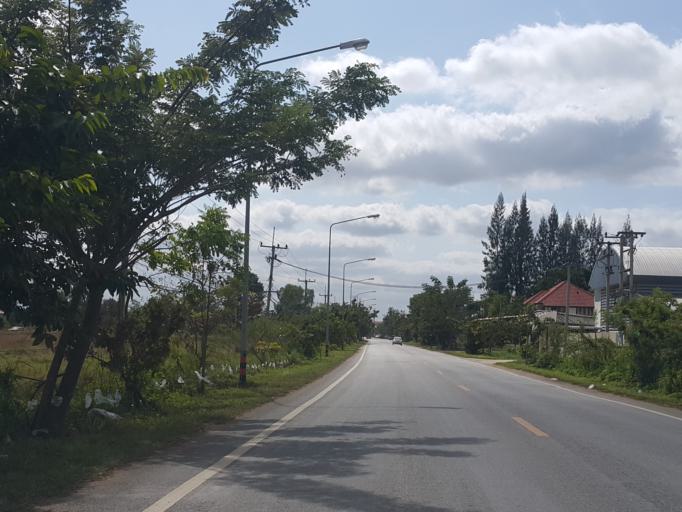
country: TH
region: Lamphun
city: Ban Thi
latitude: 18.5995
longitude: 99.0844
